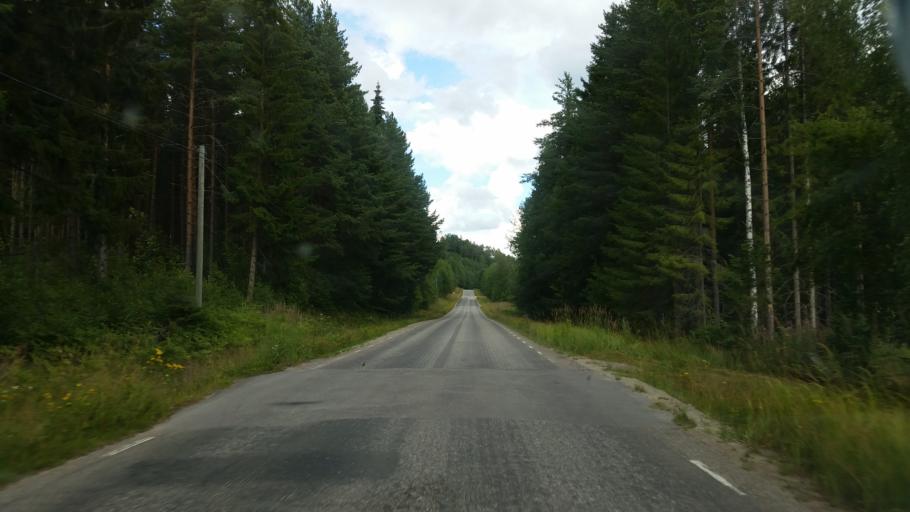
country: SE
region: Gaevleborg
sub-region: Hudiksvalls Kommun
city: Delsbo
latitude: 61.9083
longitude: 16.5688
